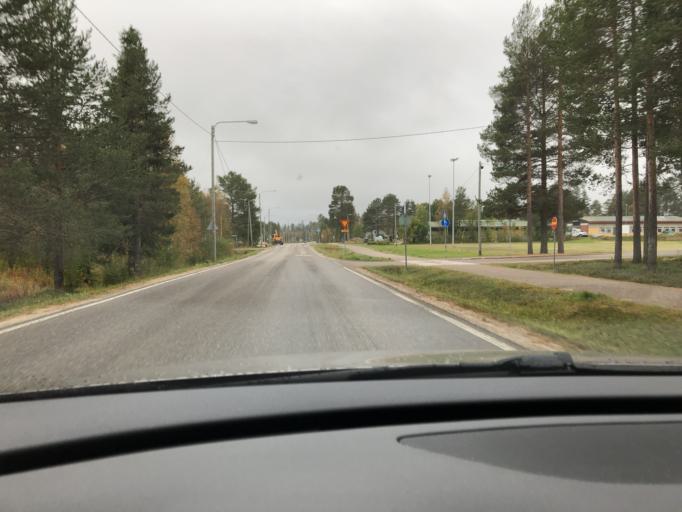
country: FI
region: Lapland
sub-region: Itae-Lappi
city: Posio
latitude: 66.1107
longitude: 28.1787
